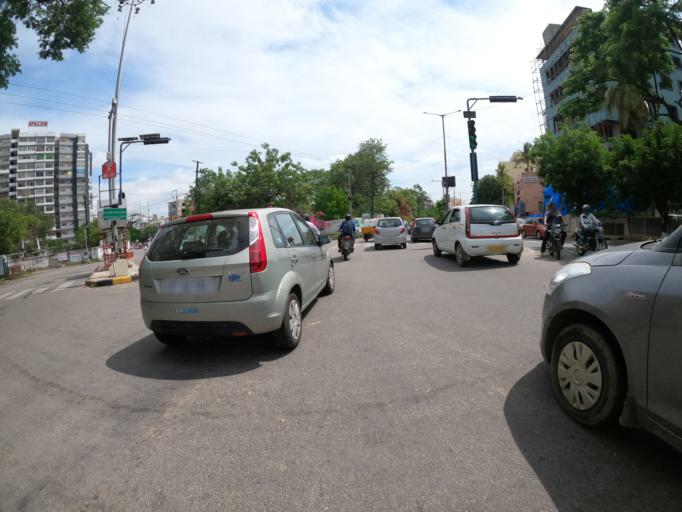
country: IN
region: Telangana
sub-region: Hyderabad
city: Hyderabad
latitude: 17.3934
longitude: 78.4268
